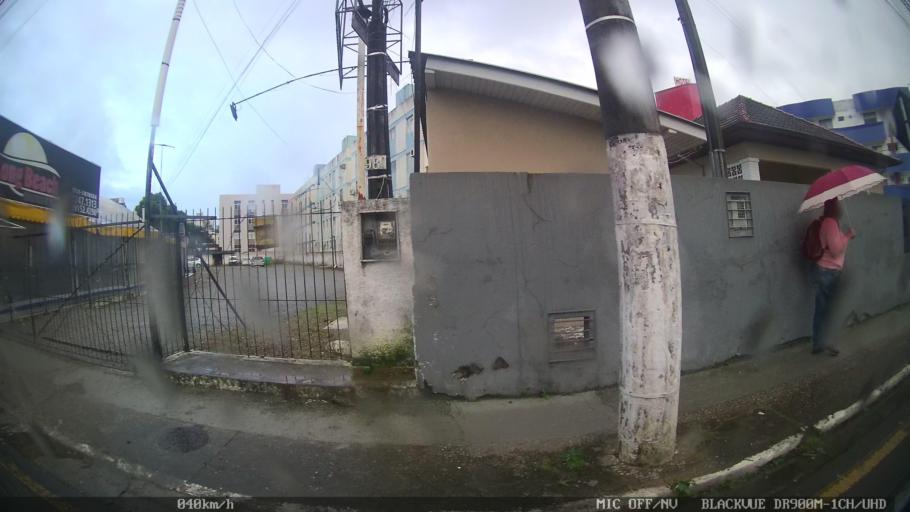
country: BR
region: Santa Catarina
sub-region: Sao Jose
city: Campinas
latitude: -27.6068
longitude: -48.6263
